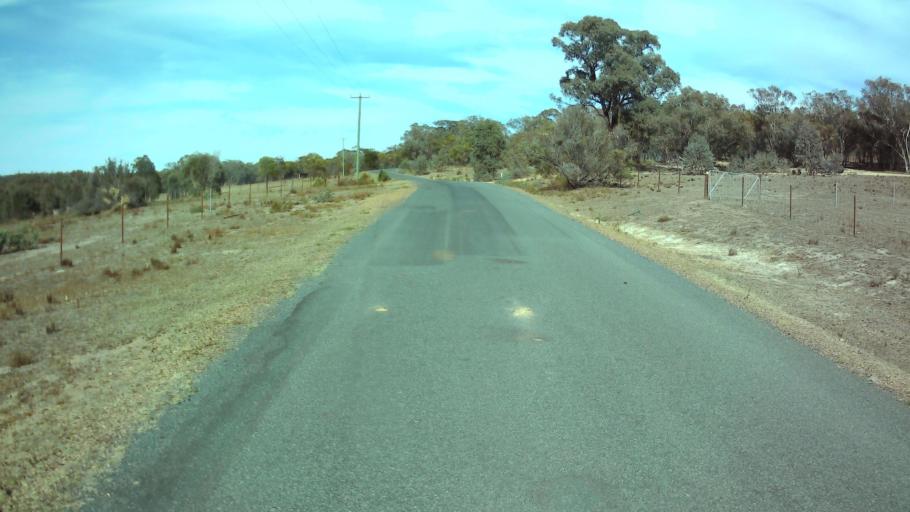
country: AU
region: New South Wales
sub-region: Weddin
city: Grenfell
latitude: -33.8788
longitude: 148.1970
